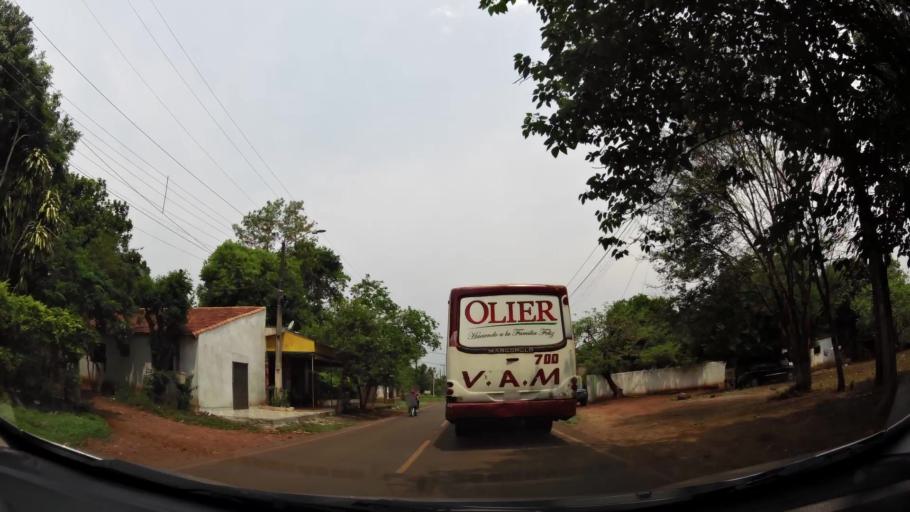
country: AR
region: Misiones
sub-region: Departamento de Iguazu
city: Puerto Iguazu
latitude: -25.5886
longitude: -54.6025
